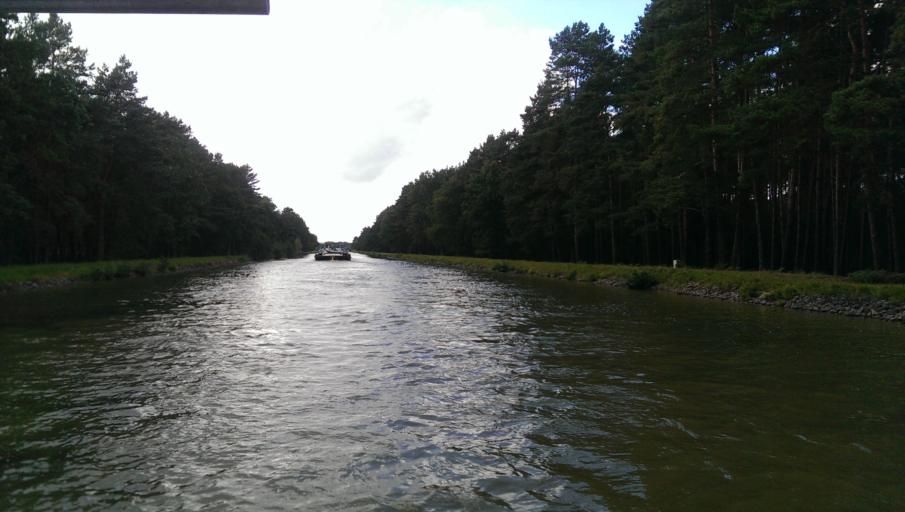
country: DE
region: Brandenburg
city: Marienwerder
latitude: 52.8542
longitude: 13.6388
